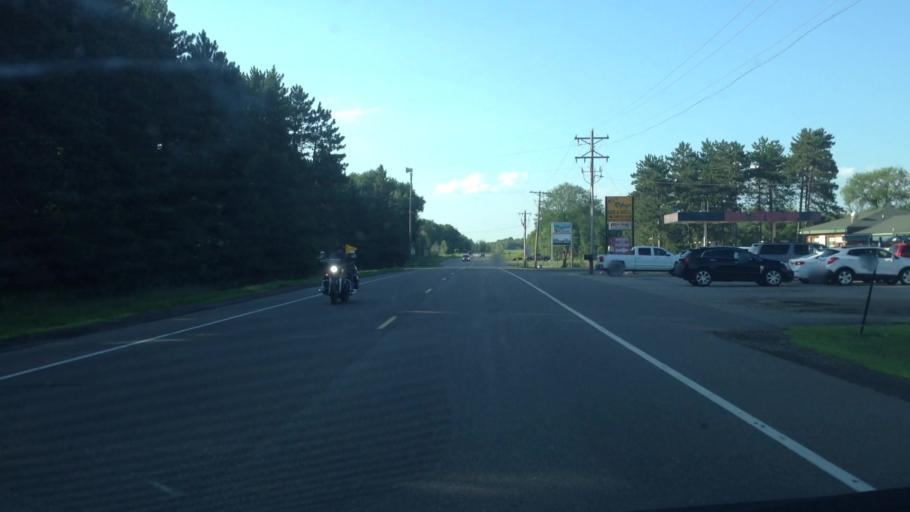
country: US
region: Minnesota
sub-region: Sherburne County
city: Big Lake
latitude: 45.4456
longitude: -93.7360
